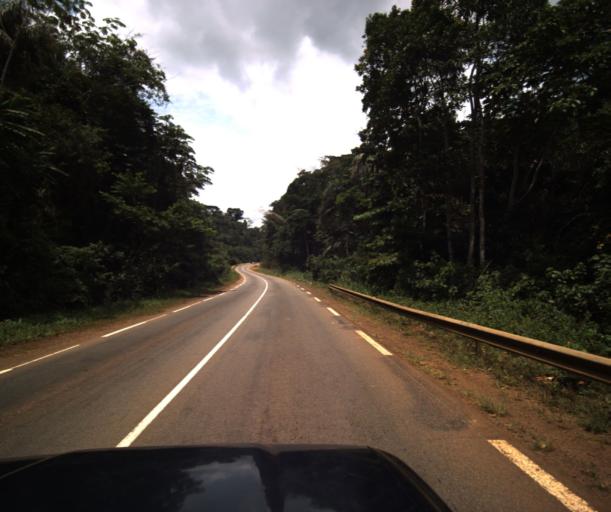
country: CM
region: Centre
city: Mbankomo
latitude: 3.7717
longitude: 11.1728
